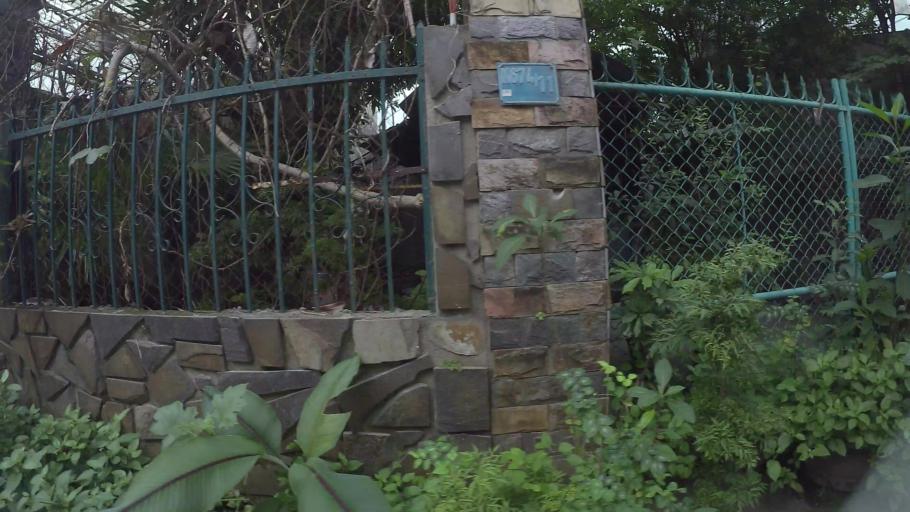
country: VN
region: Da Nang
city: Cam Le
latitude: 16.0430
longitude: 108.2056
